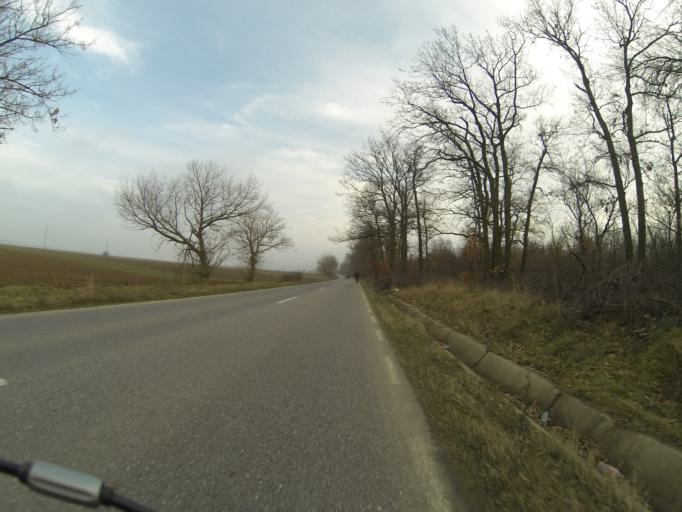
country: RO
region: Mehedinti
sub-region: Comuna Corlatel
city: Corlatel
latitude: 44.4021
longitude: 22.9050
